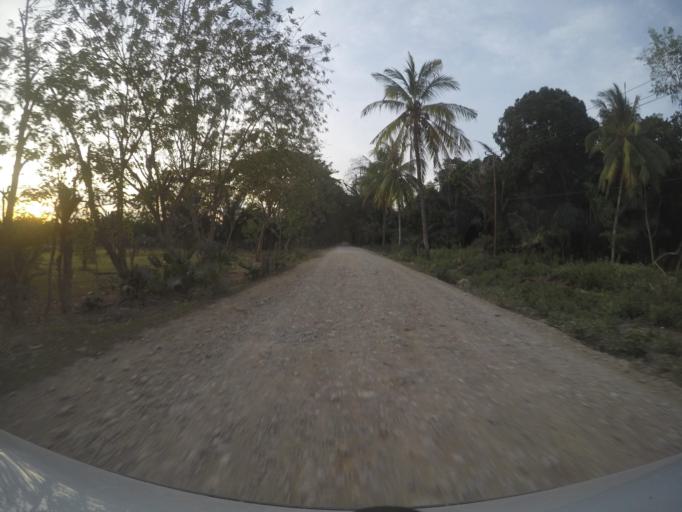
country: TL
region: Viqueque
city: Viqueque
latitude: -8.9368
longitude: 126.4140
